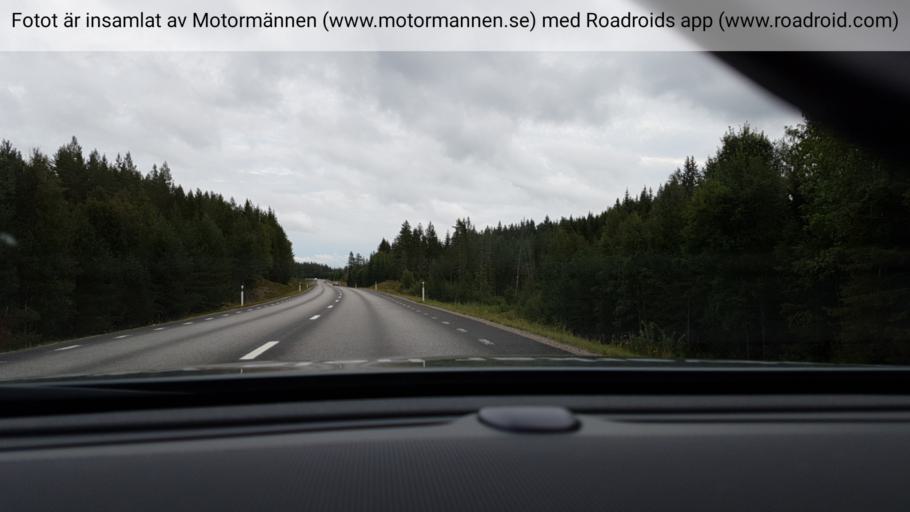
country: SE
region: Dalarna
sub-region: Faluns Kommun
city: Bjursas
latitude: 60.7492
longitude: 15.3553
